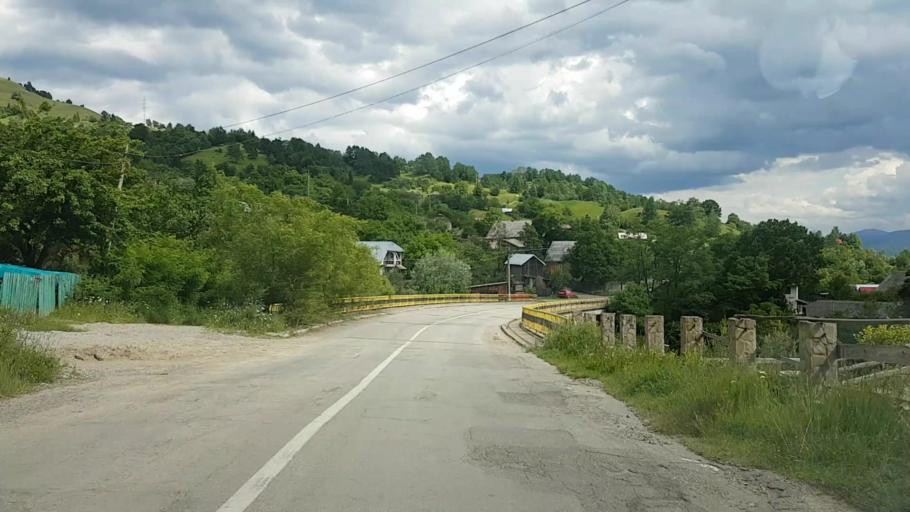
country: RO
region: Neamt
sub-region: Comuna Hangu
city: Hangu
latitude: 47.0446
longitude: 26.0530
